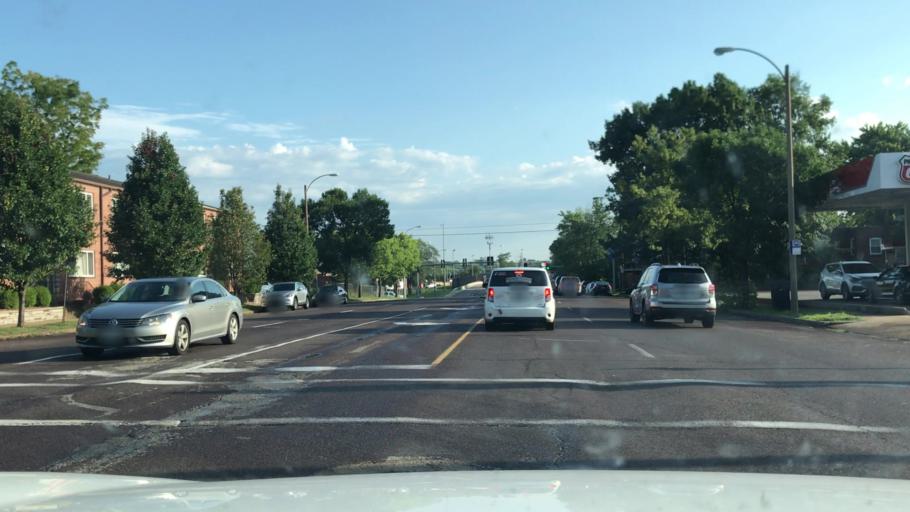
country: US
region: Missouri
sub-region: Saint Louis County
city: Maplewood
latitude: 38.6036
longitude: -90.3077
